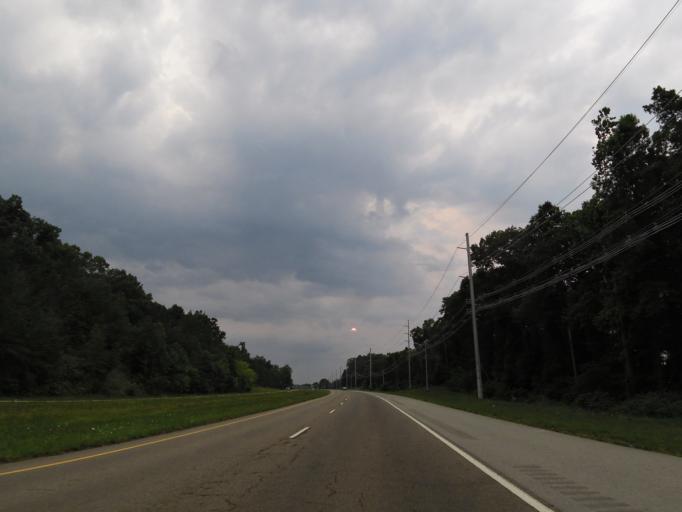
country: US
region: Tennessee
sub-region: Blount County
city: Wildwood
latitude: 35.7567
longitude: -83.8523
